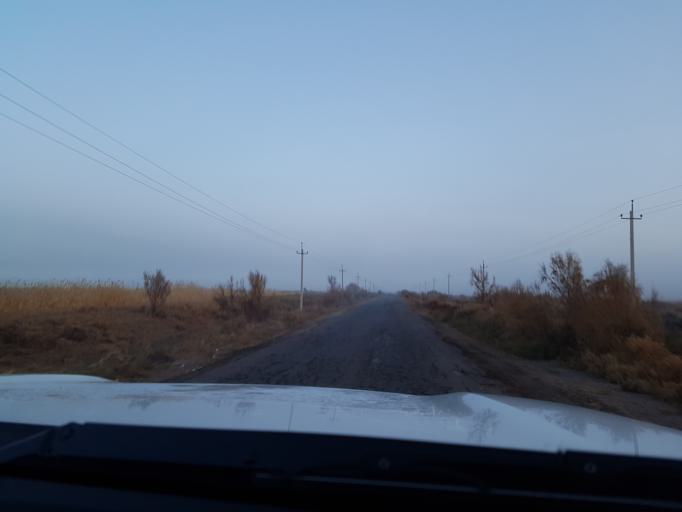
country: TM
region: Dasoguz
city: Koeneuergench
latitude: 41.7875
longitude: 58.6979
